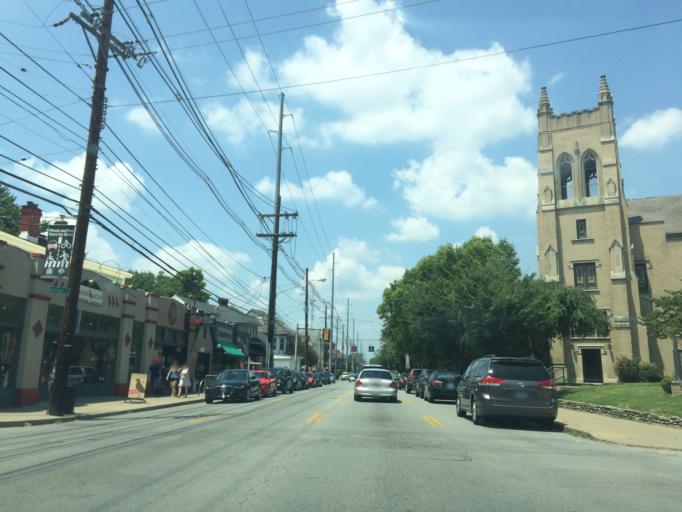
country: US
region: Kentucky
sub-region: Jefferson County
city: Audubon Park
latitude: 38.2328
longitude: -85.7107
